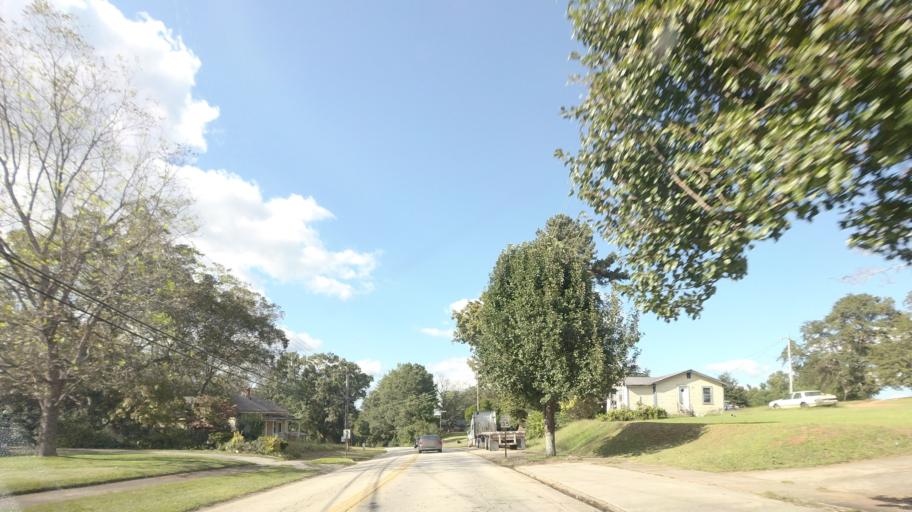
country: US
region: Georgia
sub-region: Lamar County
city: Barnesville
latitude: 33.0644
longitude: -84.1555
